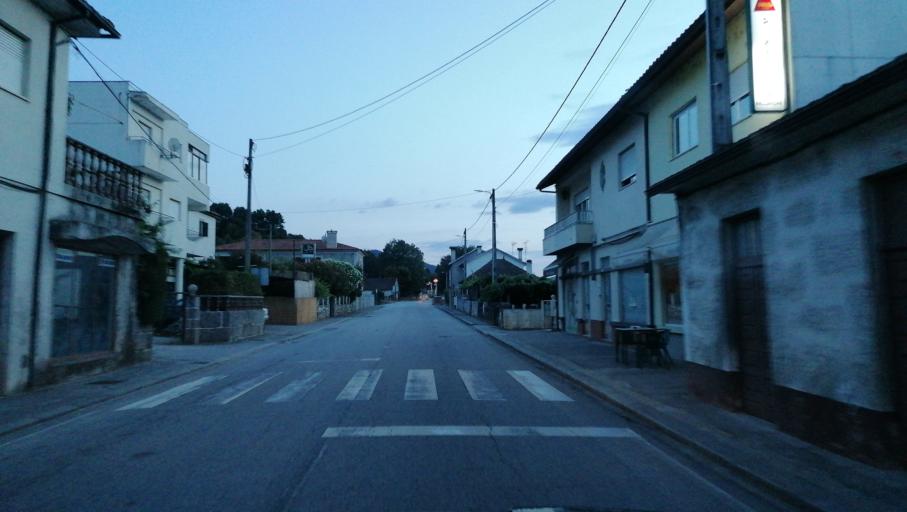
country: PT
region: Vila Real
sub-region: Vila Pouca de Aguiar
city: Vila Pouca de Aguiar
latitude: 41.5419
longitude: -7.6035
